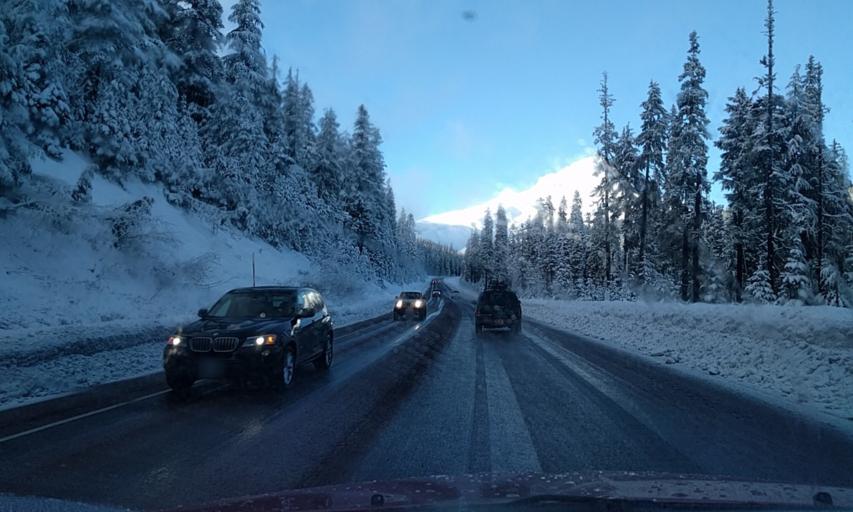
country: US
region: Oregon
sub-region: Clackamas County
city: Mount Hood Village
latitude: 45.2917
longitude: -121.6716
